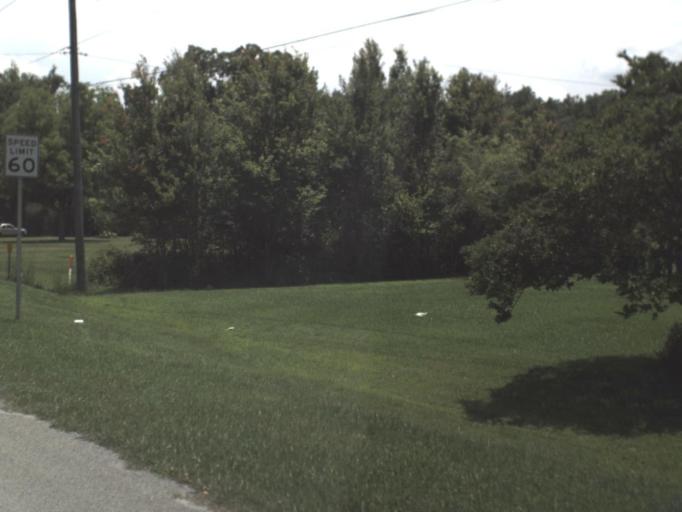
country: US
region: Florida
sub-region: Bradford County
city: Starke
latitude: 30.0131
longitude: -82.1443
